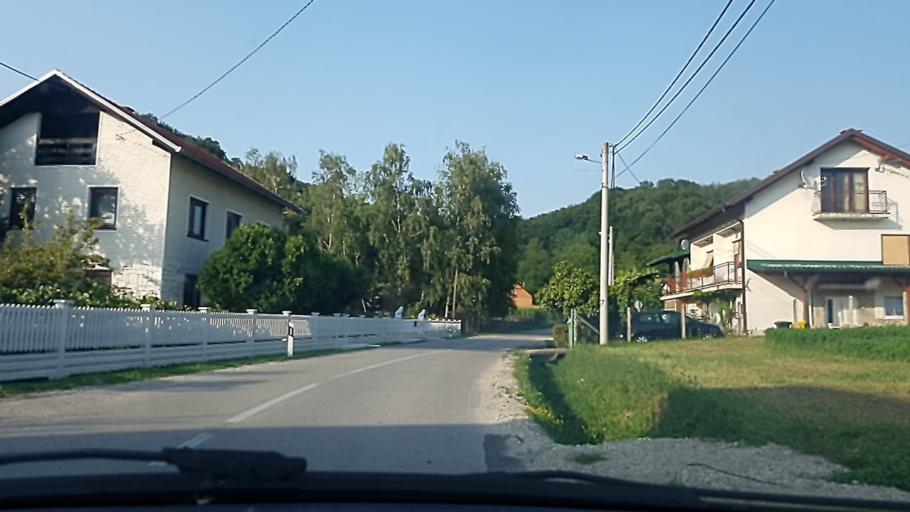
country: HR
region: Zagrebacka
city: Jakovlje
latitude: 45.9785
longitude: 15.8345
